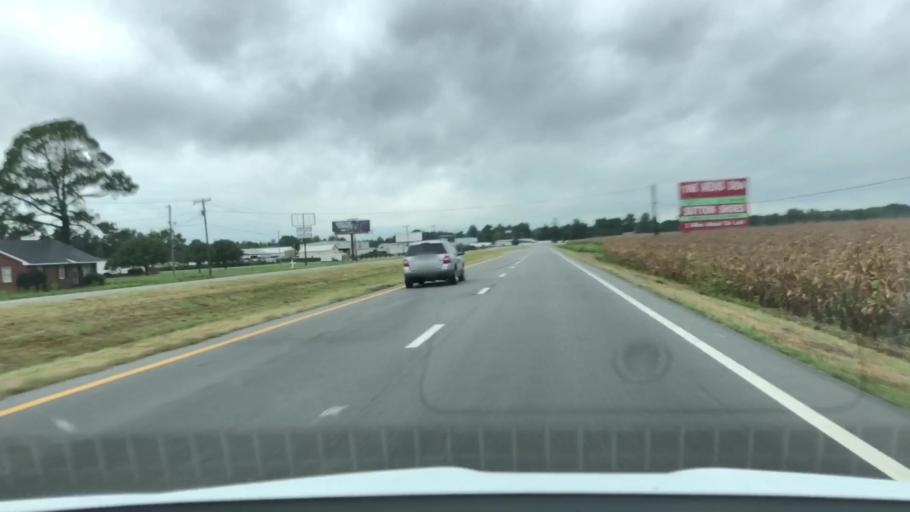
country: US
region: North Carolina
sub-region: Lenoir County
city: La Grange
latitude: 35.2678
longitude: -77.7336
